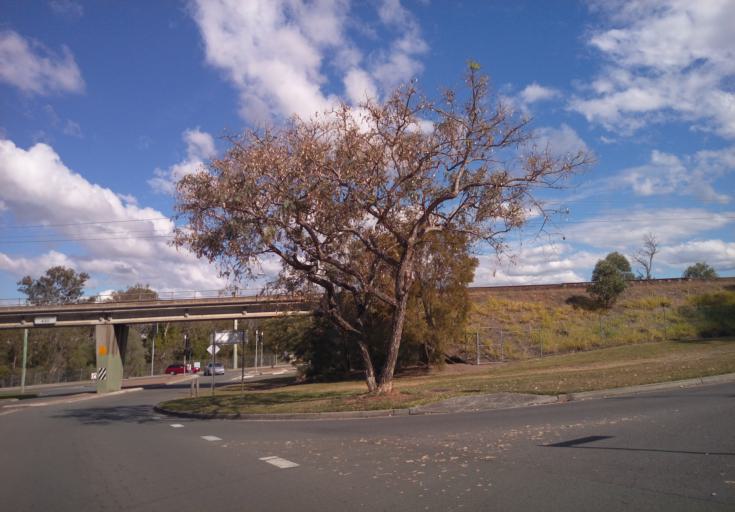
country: AU
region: Queensland
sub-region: Redland
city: Wellington Point
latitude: -27.4926
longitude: 153.2121
